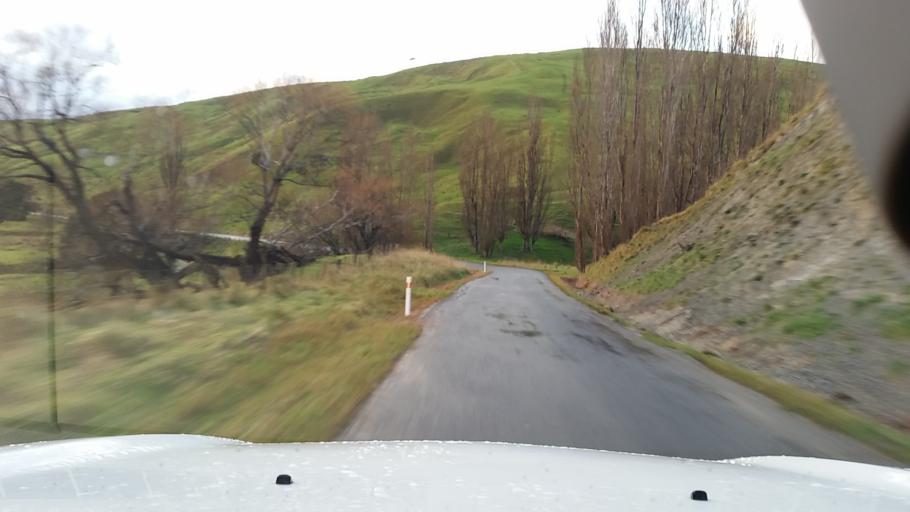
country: NZ
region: Wellington
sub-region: South Wairarapa District
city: Waipawa
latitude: -41.2902
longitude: 175.6287
